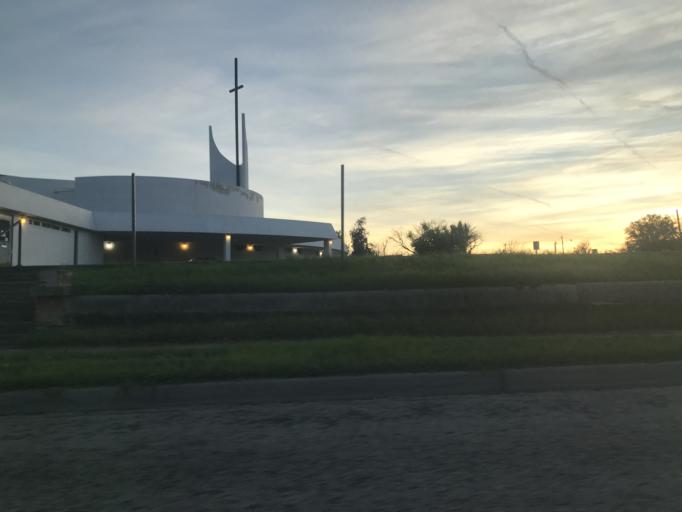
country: US
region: Texas
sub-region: Tom Green County
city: San Angelo
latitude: 31.4592
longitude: -100.4519
